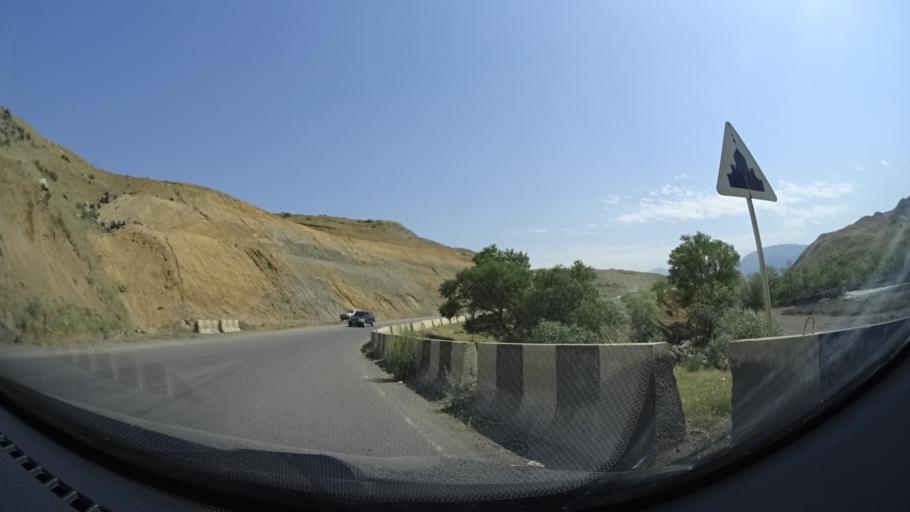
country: GE
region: Samtskhe-Javakheti
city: Aspindza
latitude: 41.5927
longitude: 43.1798
